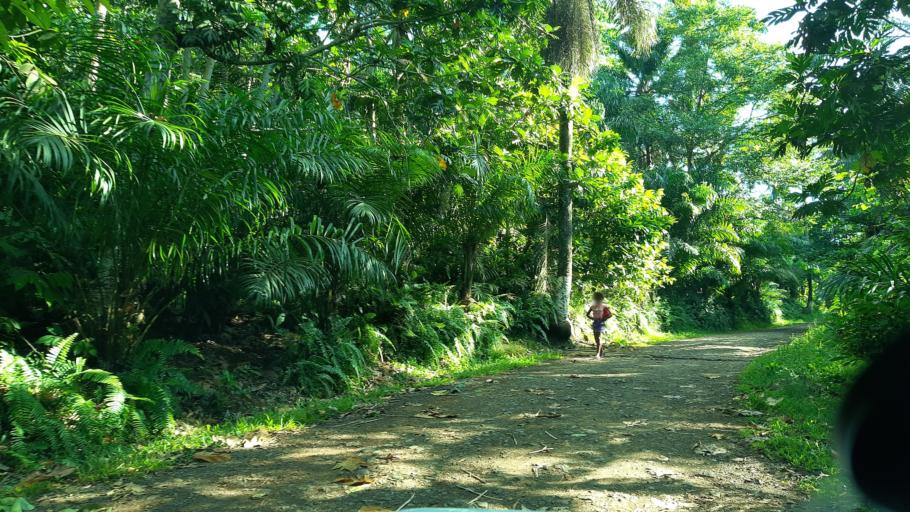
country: ST
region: Sao Tome Island
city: Sao Tome
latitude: 0.2448
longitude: 6.7381
